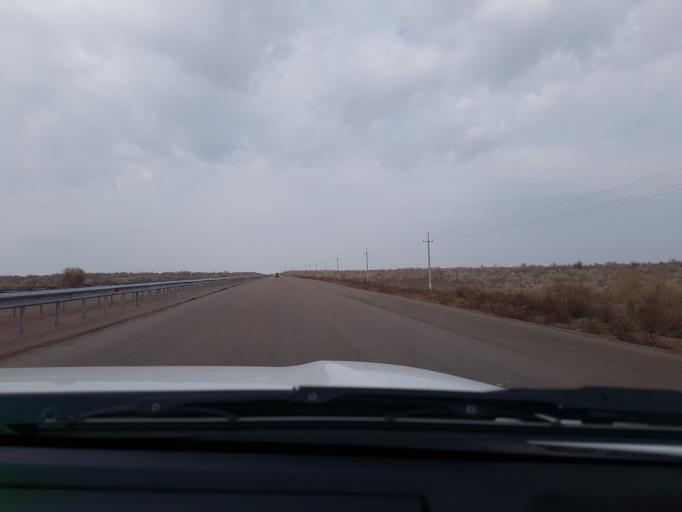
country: TM
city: Akdepe
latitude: 41.7366
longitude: 59.0298
